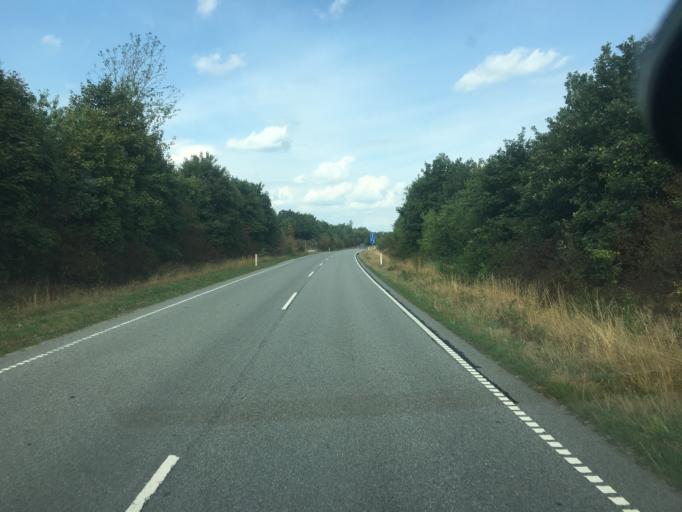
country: DK
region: South Denmark
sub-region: Aabenraa Kommune
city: Tinglev
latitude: 54.9411
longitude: 9.2951
